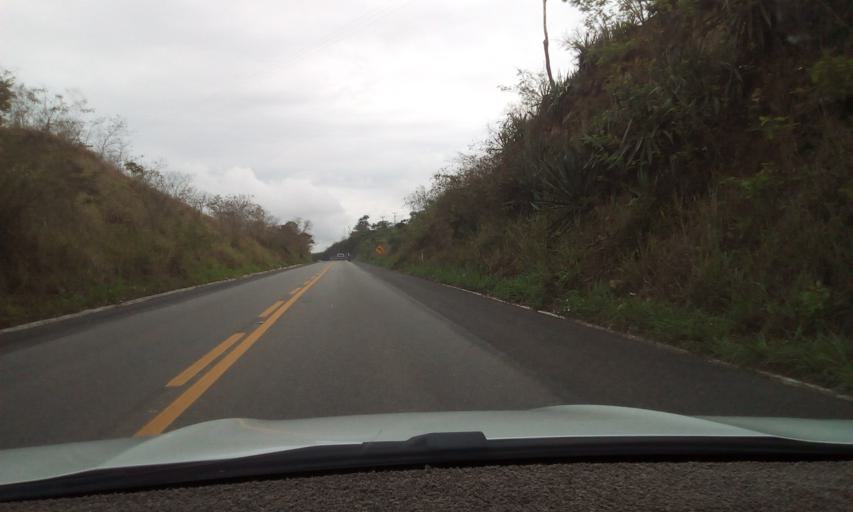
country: BR
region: Paraiba
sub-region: Lagoa Seca
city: Lagoa Seca
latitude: -7.1926
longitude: -35.8700
